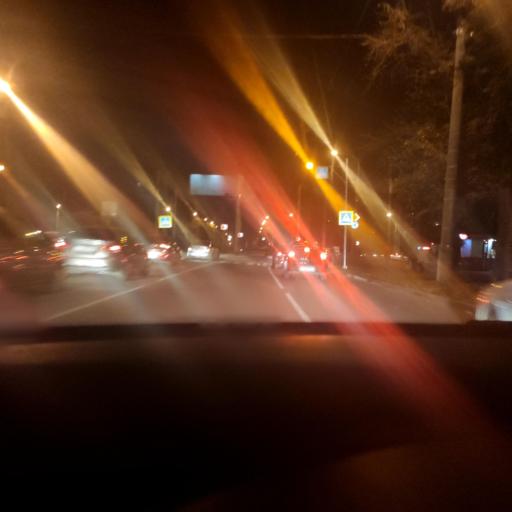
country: RU
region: Samara
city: Samara
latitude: 53.2296
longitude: 50.2059
